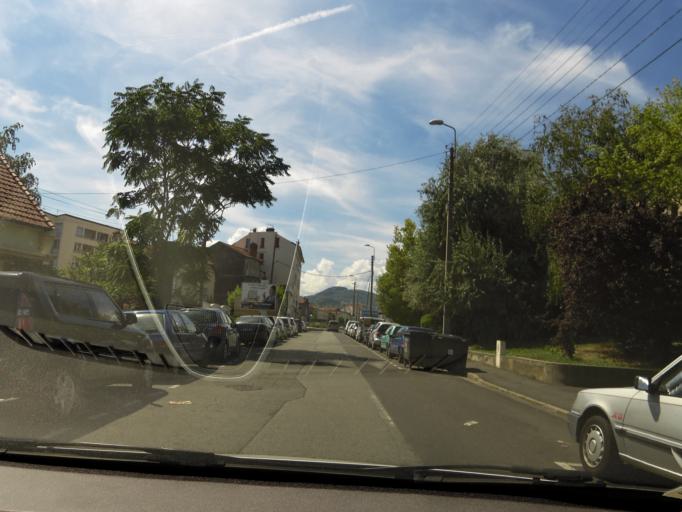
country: FR
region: Auvergne
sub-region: Departement du Puy-de-Dome
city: Clermont-Ferrand
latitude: 45.7783
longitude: 3.1042
